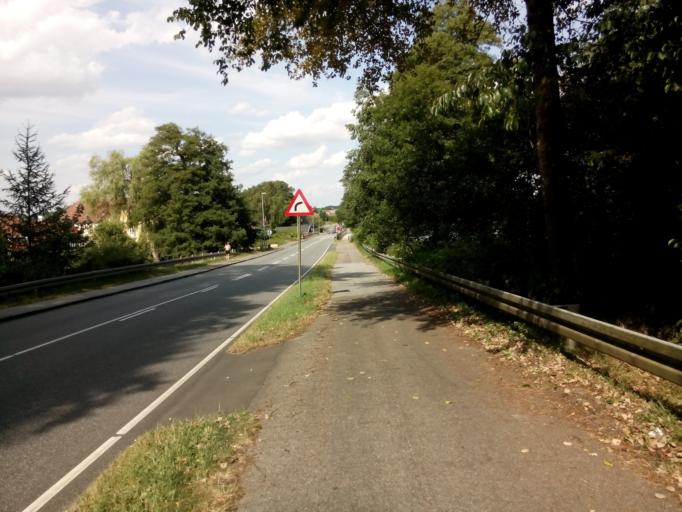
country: DK
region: Central Jutland
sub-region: Skanderborg Kommune
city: Ry
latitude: 56.0907
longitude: 9.7525
